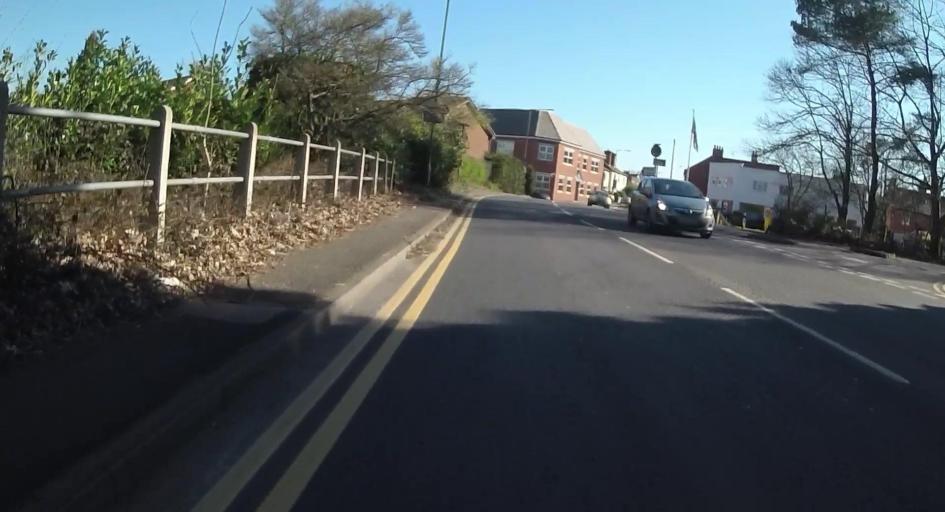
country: GB
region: England
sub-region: Royal Borough of Windsor and Maidenhead
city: Ascot
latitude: 51.4047
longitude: -0.6720
